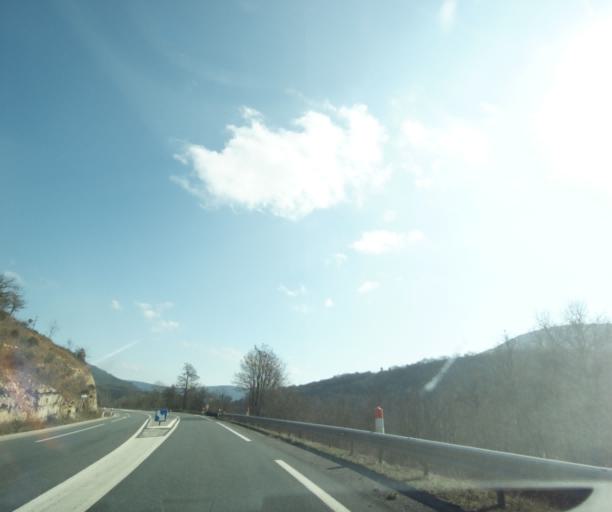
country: FR
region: Languedoc-Roussillon
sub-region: Departement de la Lozere
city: Chanac
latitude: 44.4842
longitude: 3.2992
